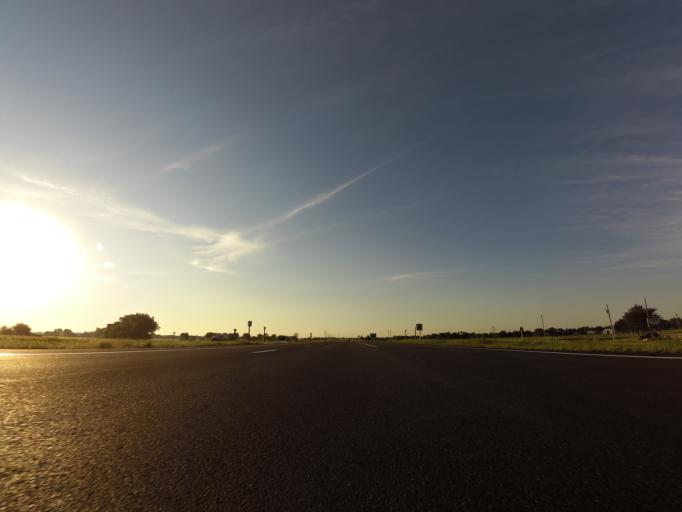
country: US
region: Kansas
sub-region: Sedgwick County
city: Maize
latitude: 37.7956
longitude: -97.4821
